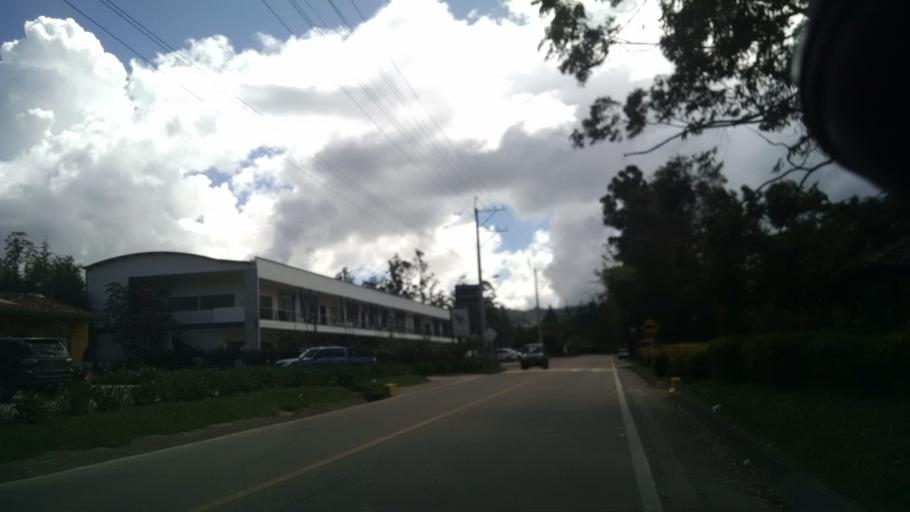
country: CO
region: Antioquia
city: El Retiro
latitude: 6.0734
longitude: -75.4975
